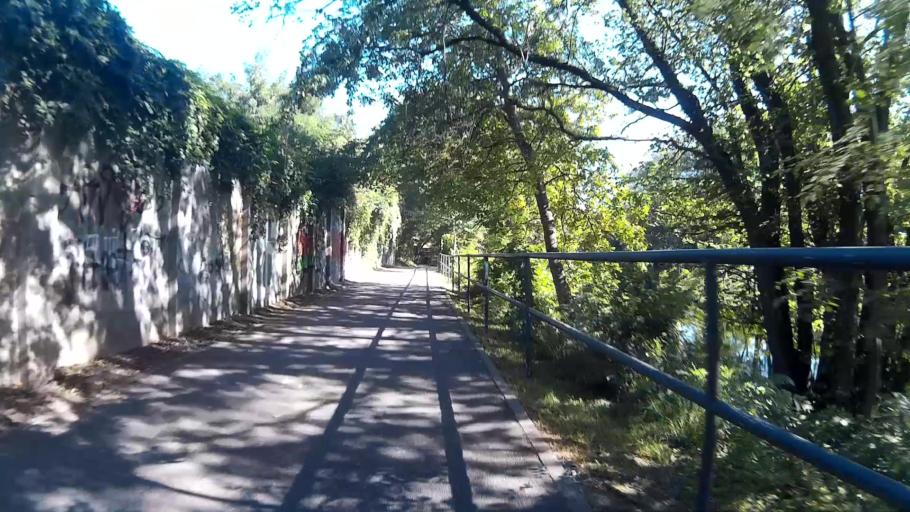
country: CZ
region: South Moravian
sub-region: Mesto Brno
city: Brno
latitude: 49.1804
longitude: 16.6121
